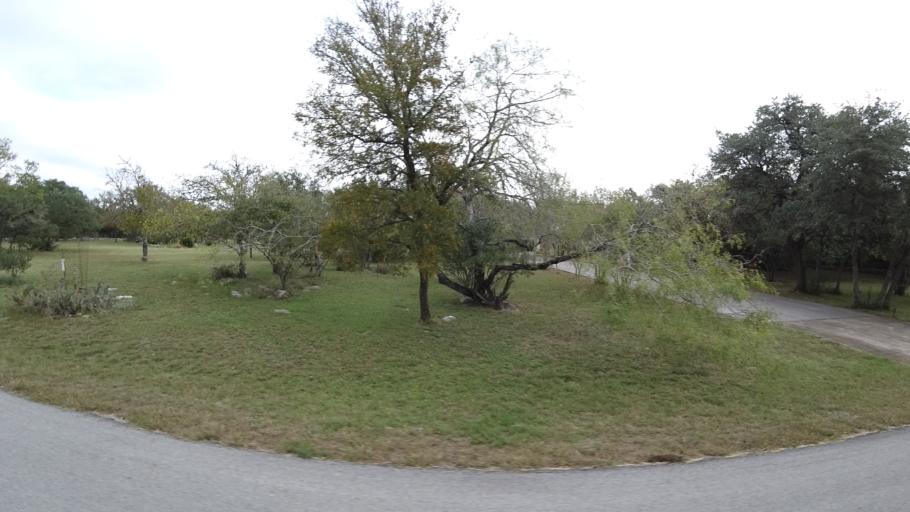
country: US
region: Texas
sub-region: Travis County
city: Shady Hollow
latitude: 30.1466
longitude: -97.8808
